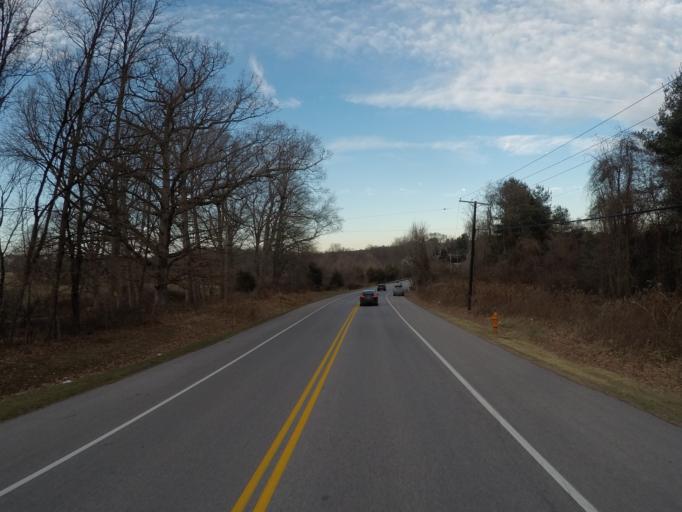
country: US
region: Maryland
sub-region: Howard County
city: Columbia
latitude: 39.2392
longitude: -76.8686
